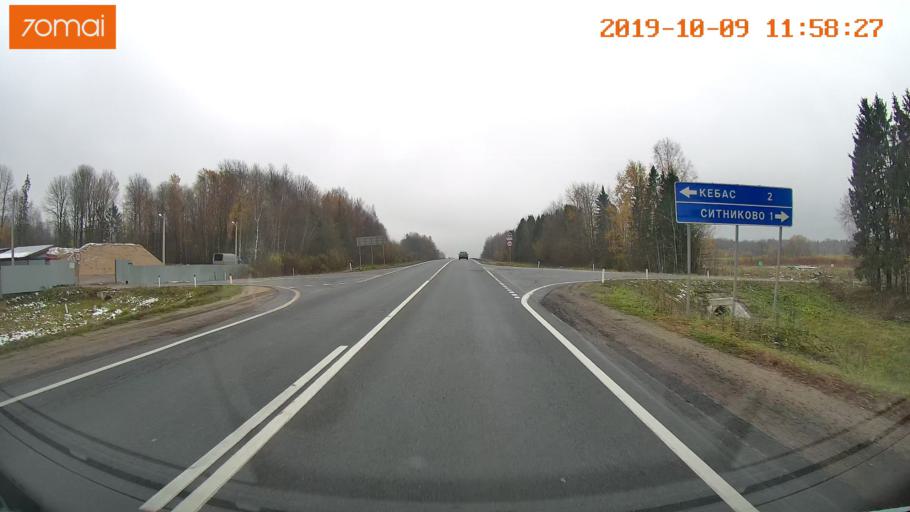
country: RU
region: Vologda
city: Gryazovets
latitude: 58.7179
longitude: 40.2965
